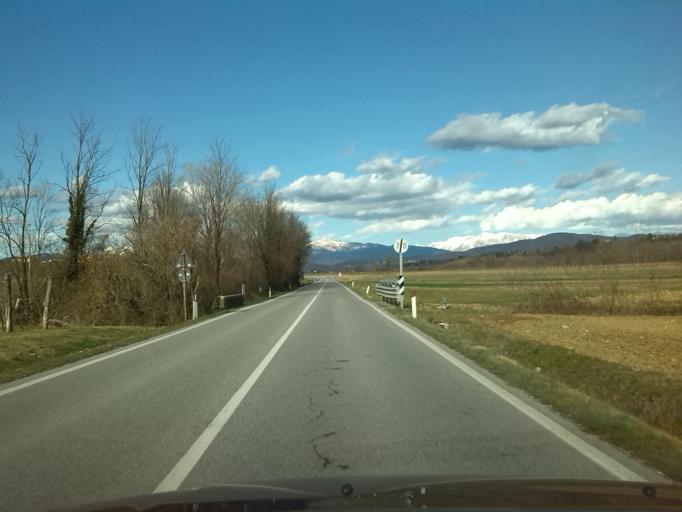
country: IT
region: Friuli Venezia Giulia
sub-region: Provincia di Udine
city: Corno di Rosazzo
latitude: 46.0116
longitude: 13.4370
